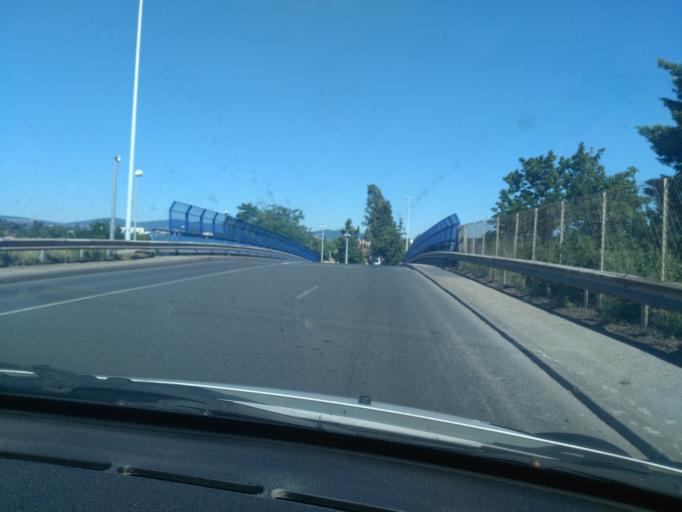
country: FR
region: Rhone-Alpes
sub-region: Departement du Rhone
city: Villefranche-sur-Saone
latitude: 45.9785
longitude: 4.7368
